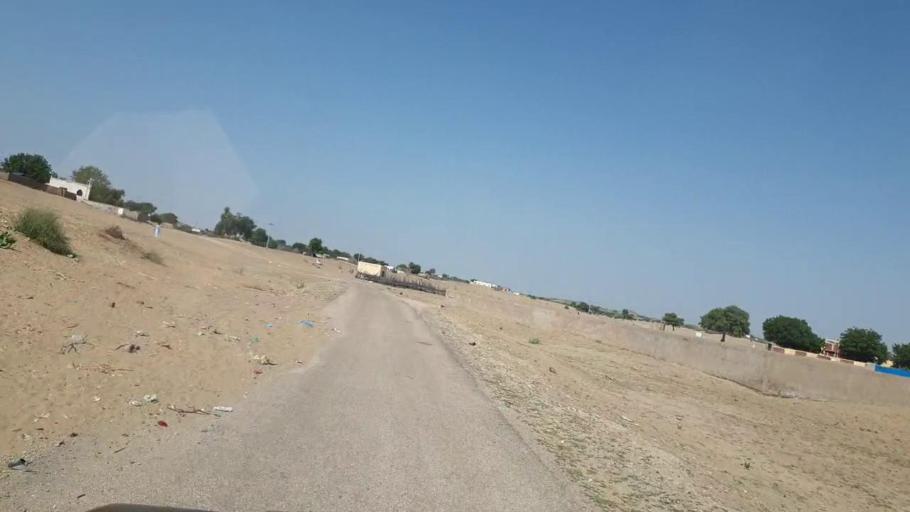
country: PK
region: Sindh
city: Chor
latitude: 25.6455
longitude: 70.3207
